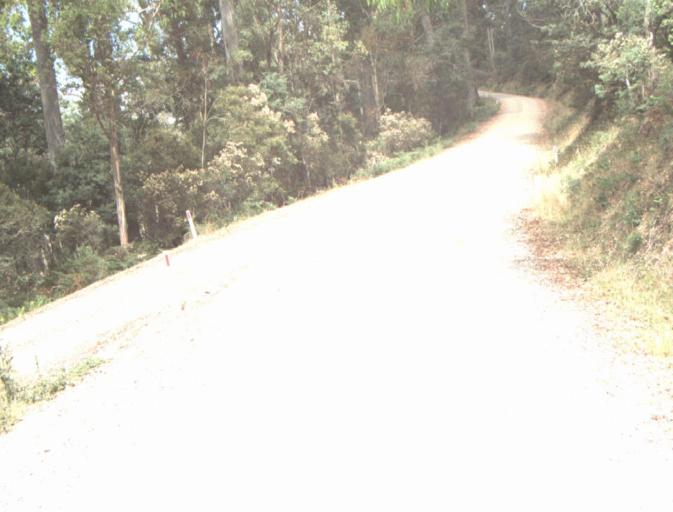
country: AU
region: Tasmania
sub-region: Dorset
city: Scottsdale
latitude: -41.4172
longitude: 147.5226
